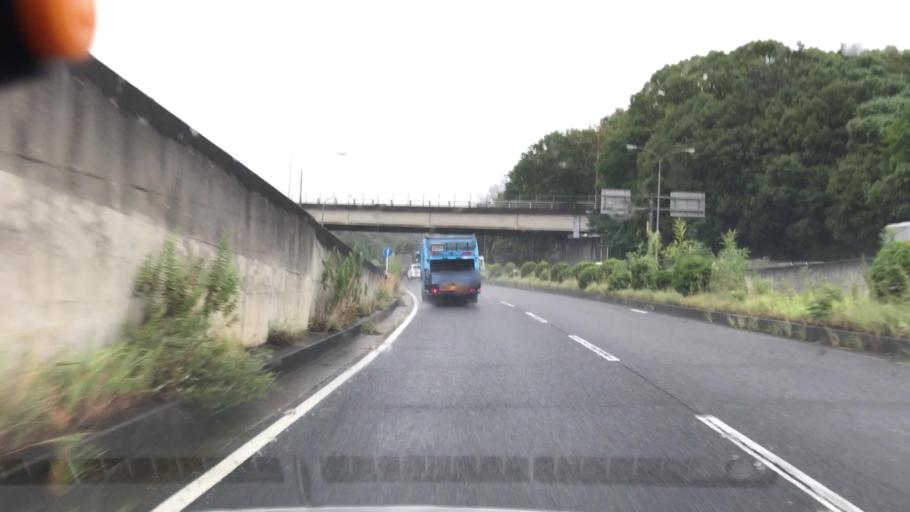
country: JP
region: Nara
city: Nara-shi
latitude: 34.7077
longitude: 135.8063
